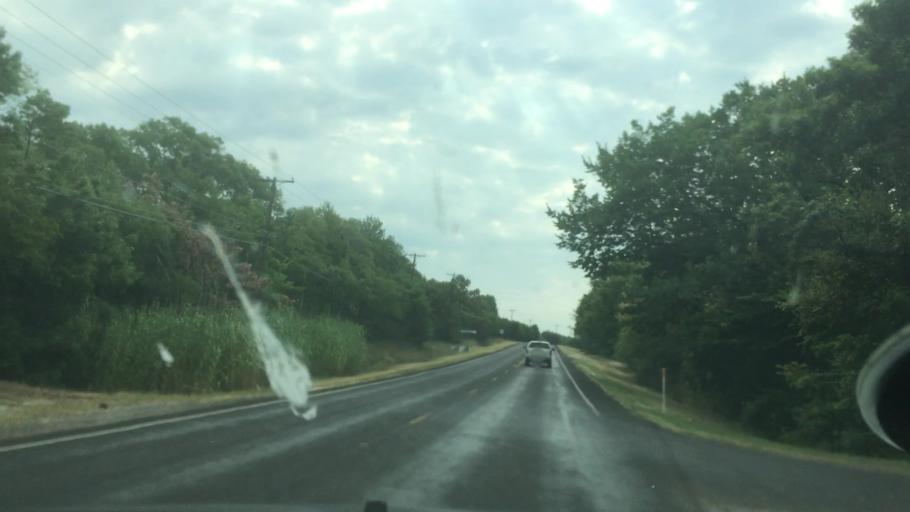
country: US
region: Texas
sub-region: Grayson County
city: Denison
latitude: 33.7840
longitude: -96.5931
